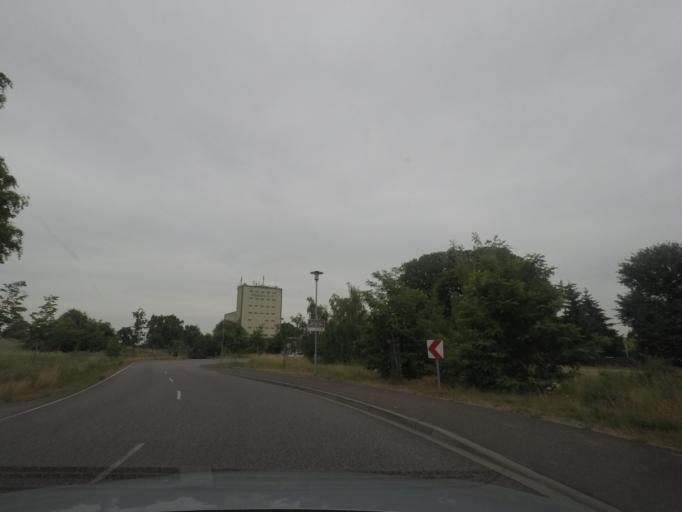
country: DE
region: Saxony-Anhalt
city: Seehausen
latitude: 52.1082
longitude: 11.2837
